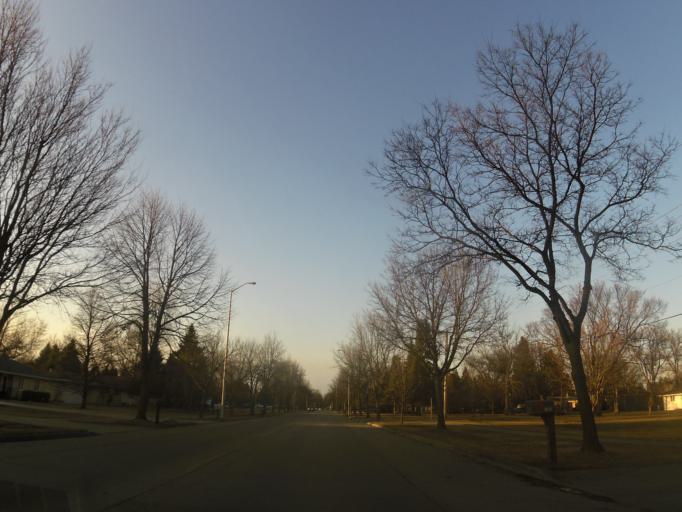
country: US
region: North Dakota
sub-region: Grand Forks County
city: Grand Forks
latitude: 47.8856
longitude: -97.0291
